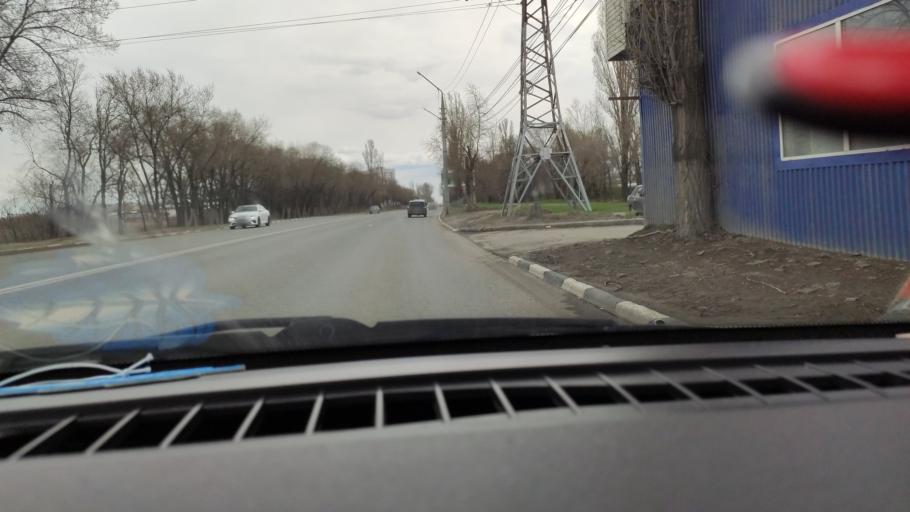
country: RU
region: Saratov
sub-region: Saratovskiy Rayon
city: Saratov
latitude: 51.5751
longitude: 45.9893
